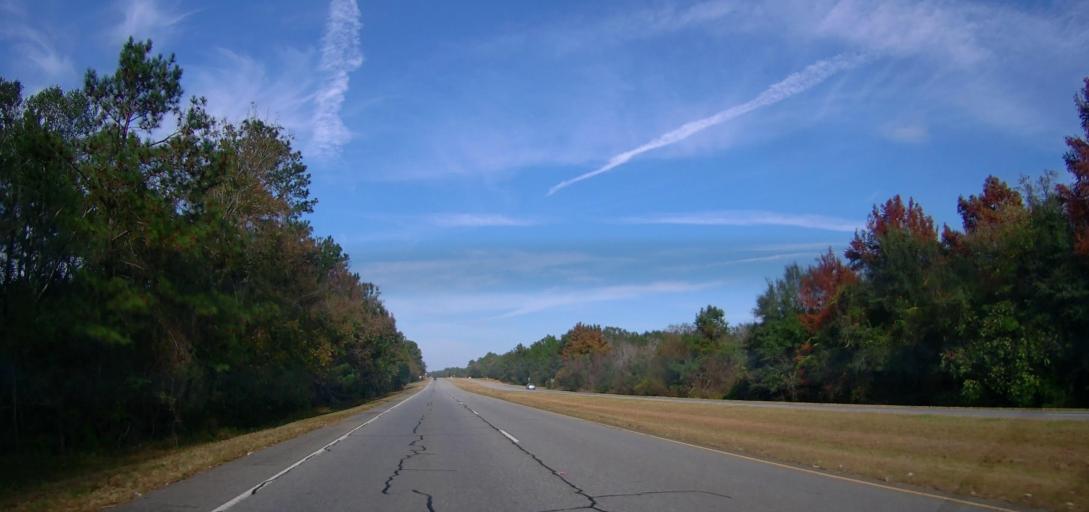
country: US
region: Georgia
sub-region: Mitchell County
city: Camilla
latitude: 31.3071
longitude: -84.1785
